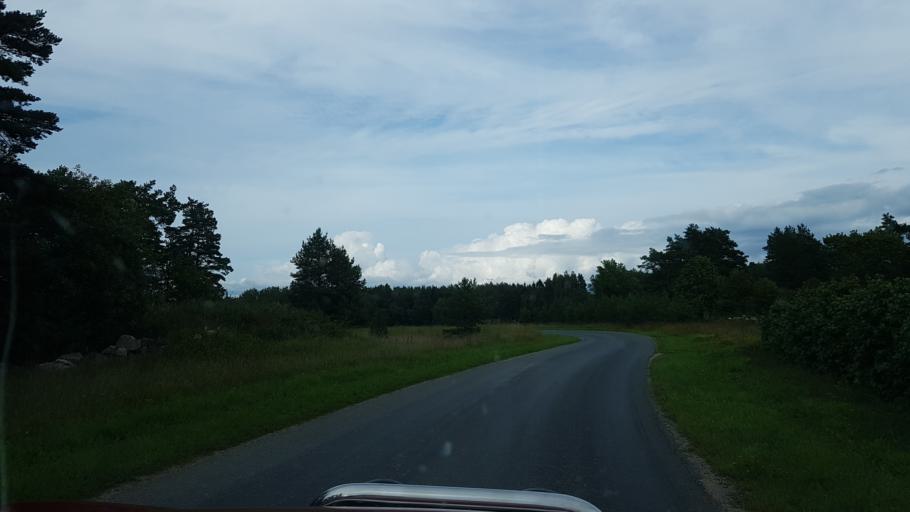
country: EE
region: Laeaene
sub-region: Ridala Parish
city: Uuemoisa
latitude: 59.0099
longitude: 23.7238
